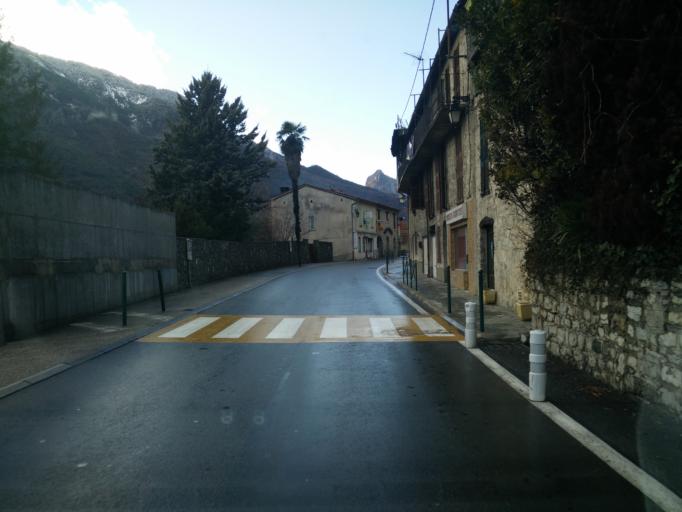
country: FR
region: Provence-Alpes-Cote d'Azur
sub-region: Departement des Alpes-Maritimes
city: Puget-Theniers
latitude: 43.9479
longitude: 7.0083
